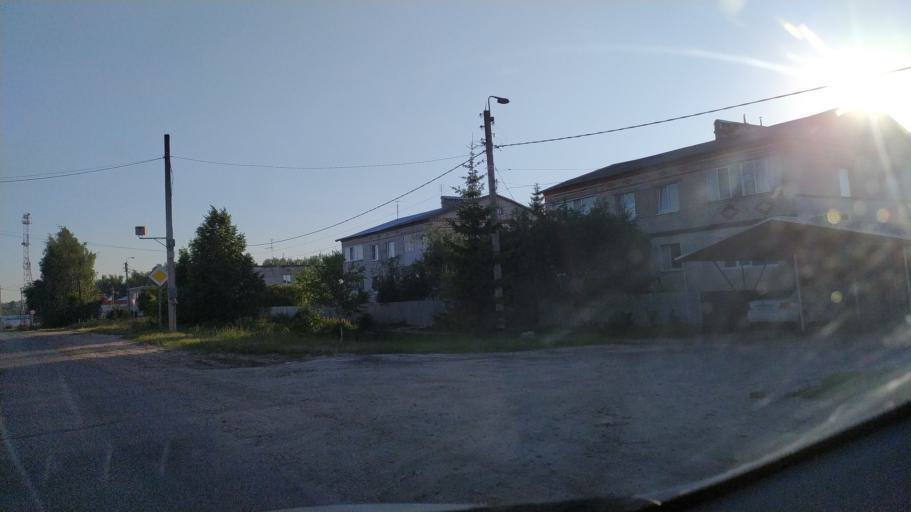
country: RU
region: Chuvashia
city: Kugesi
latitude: 56.0372
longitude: 47.3156
